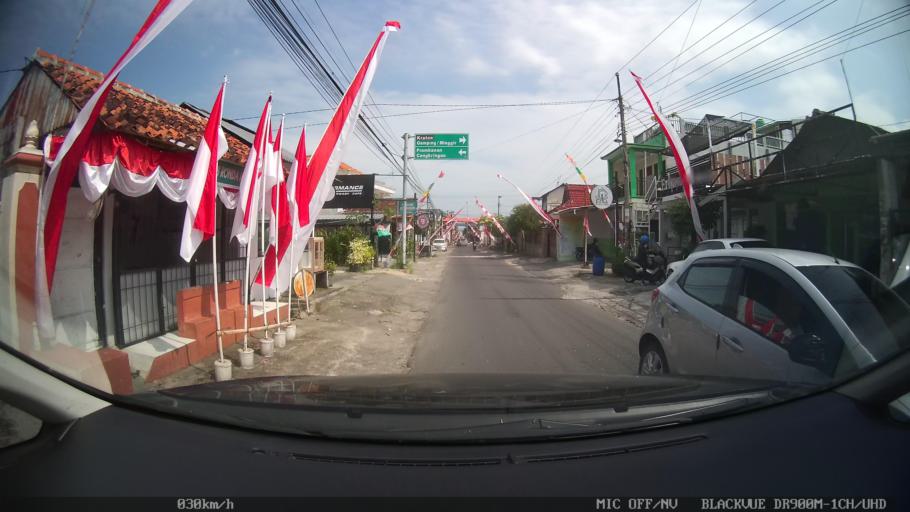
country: ID
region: Daerah Istimewa Yogyakarta
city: Depok
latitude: -7.7628
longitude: 110.4224
